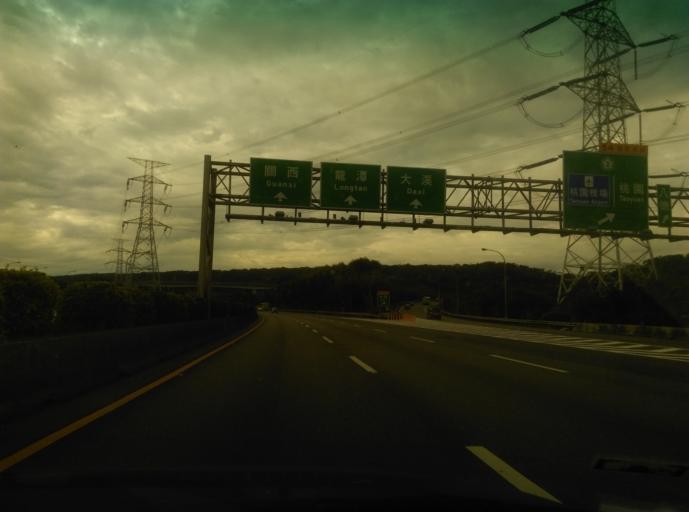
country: TW
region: Taiwan
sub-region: Taoyuan
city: Taoyuan
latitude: 24.9396
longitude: 121.3294
